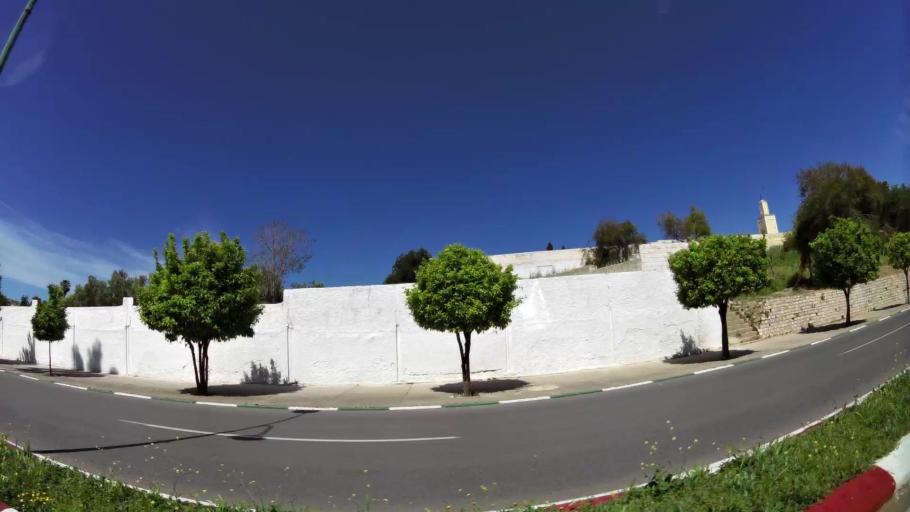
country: MA
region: Meknes-Tafilalet
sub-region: Meknes
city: Meknes
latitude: 33.8891
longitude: -5.5528
